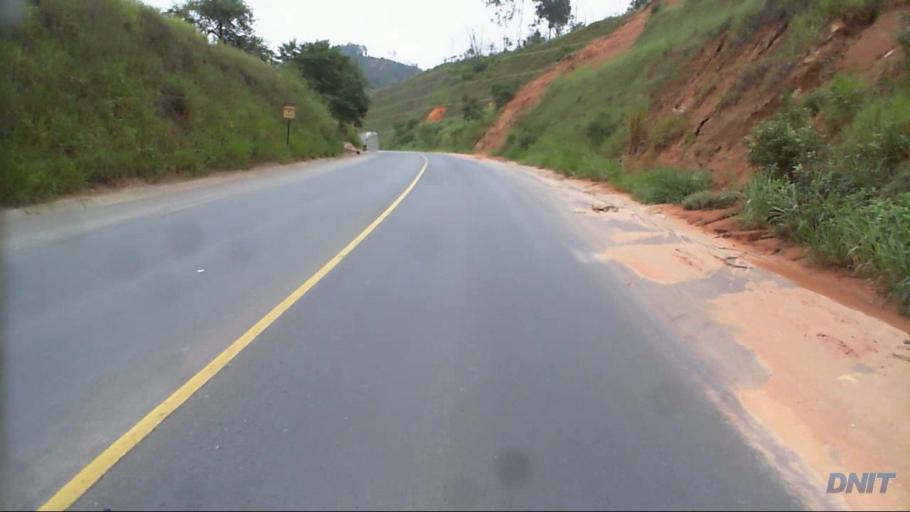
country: BR
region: Minas Gerais
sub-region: Coronel Fabriciano
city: Coronel Fabriciano
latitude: -19.5266
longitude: -42.6684
